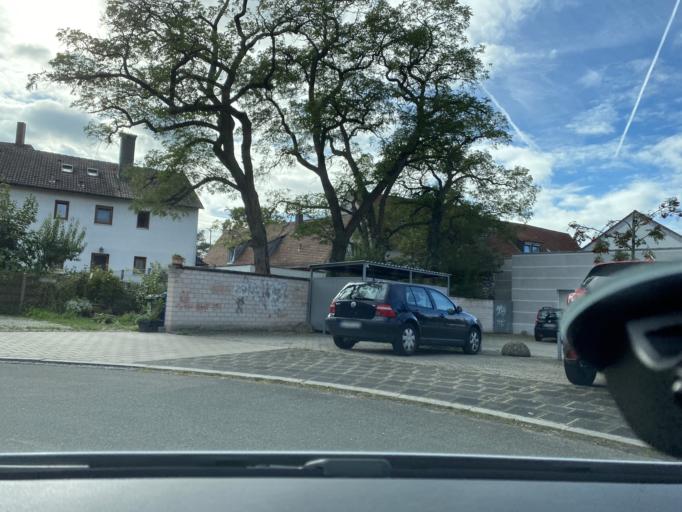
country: DE
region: Bavaria
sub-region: Regierungsbezirk Mittelfranken
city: Furth
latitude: 49.4902
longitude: 10.9963
